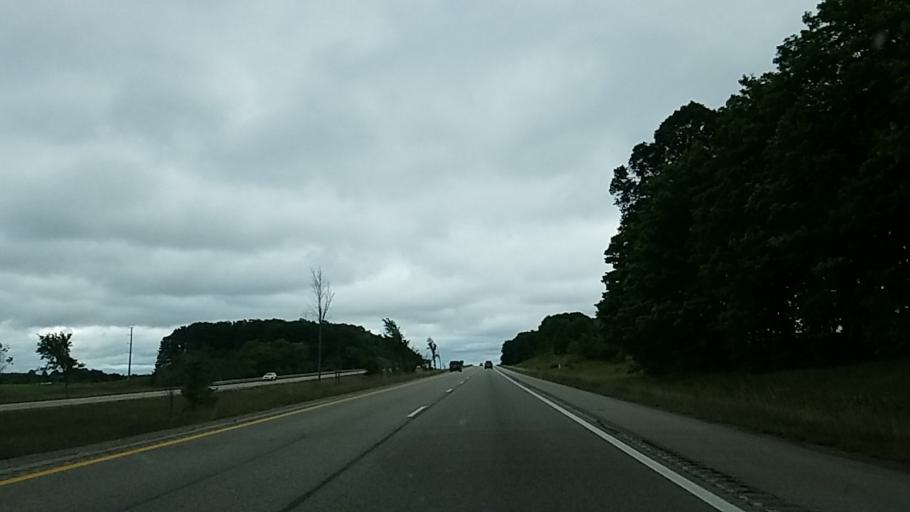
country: US
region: Michigan
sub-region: Otsego County
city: Gaylord
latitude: 45.0672
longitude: -84.6892
